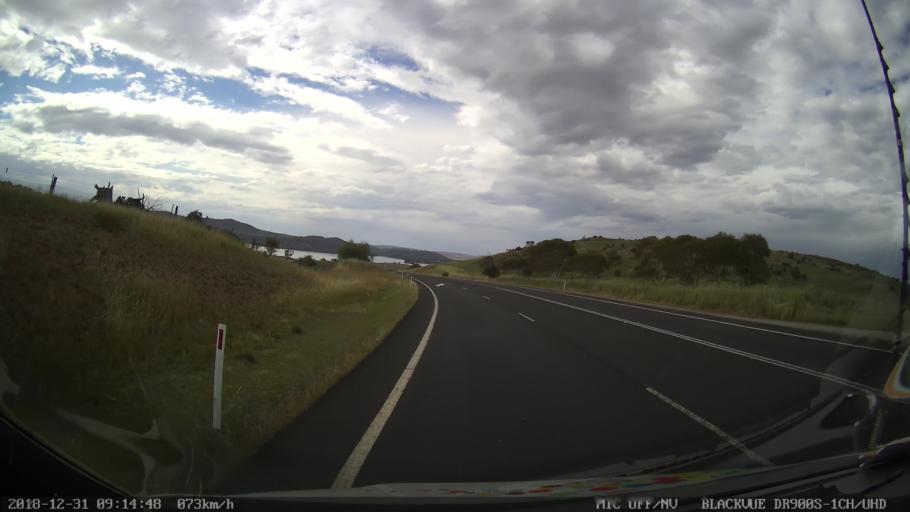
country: AU
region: New South Wales
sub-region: Snowy River
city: Jindabyne
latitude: -36.3786
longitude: 148.5947
